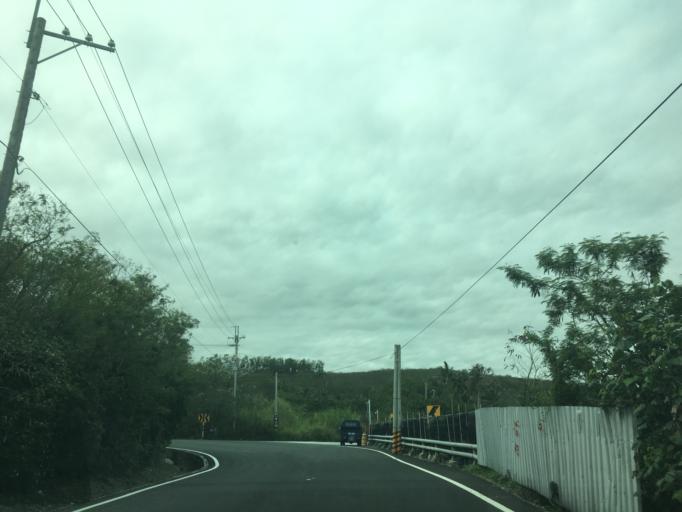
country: TW
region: Taiwan
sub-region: Taitung
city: Taitung
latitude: 22.7912
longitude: 121.1617
